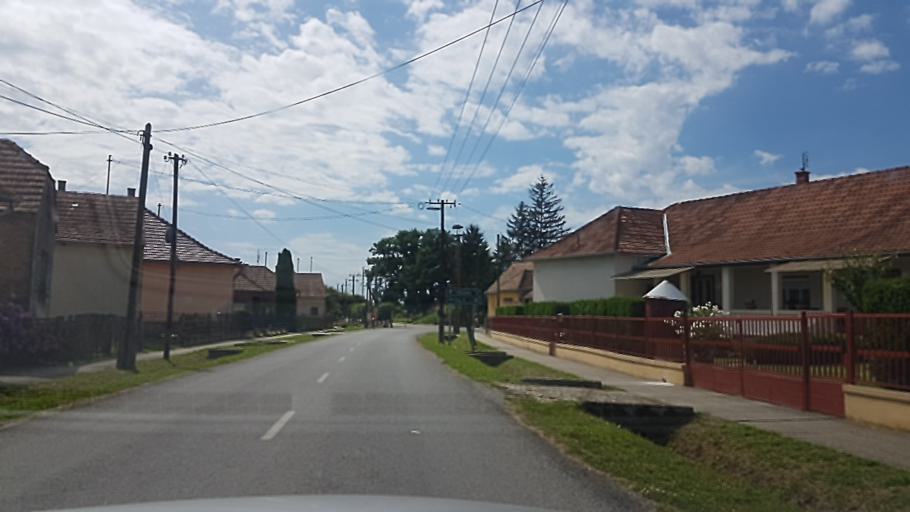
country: HU
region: Somogy
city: Barcs
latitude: 45.9308
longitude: 17.6473
